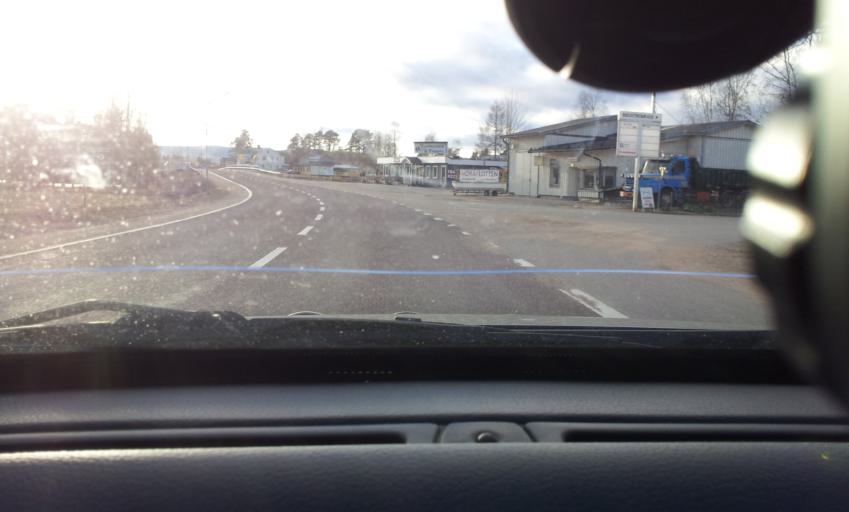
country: SE
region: Jaemtland
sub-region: Harjedalens Kommun
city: Sveg
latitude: 62.1730
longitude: 14.9478
